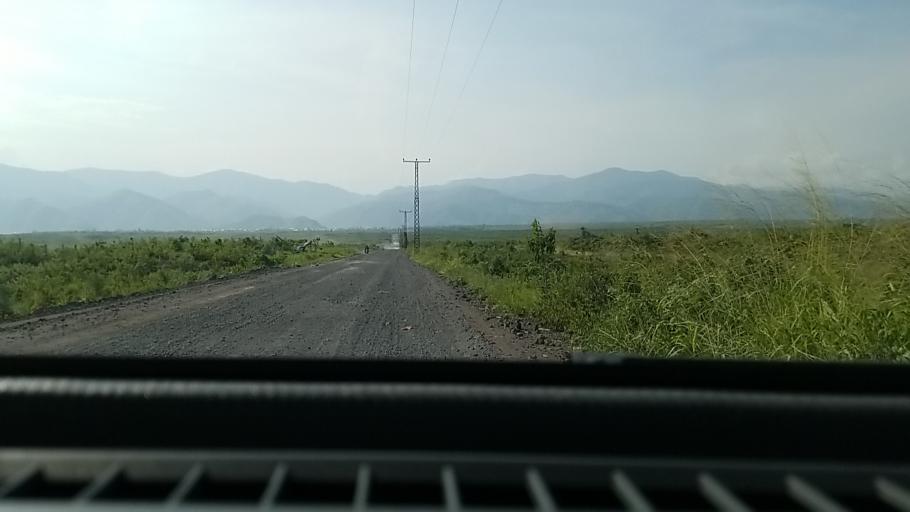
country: CD
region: Nord Kivu
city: Sake
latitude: -1.5876
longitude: 29.0915
